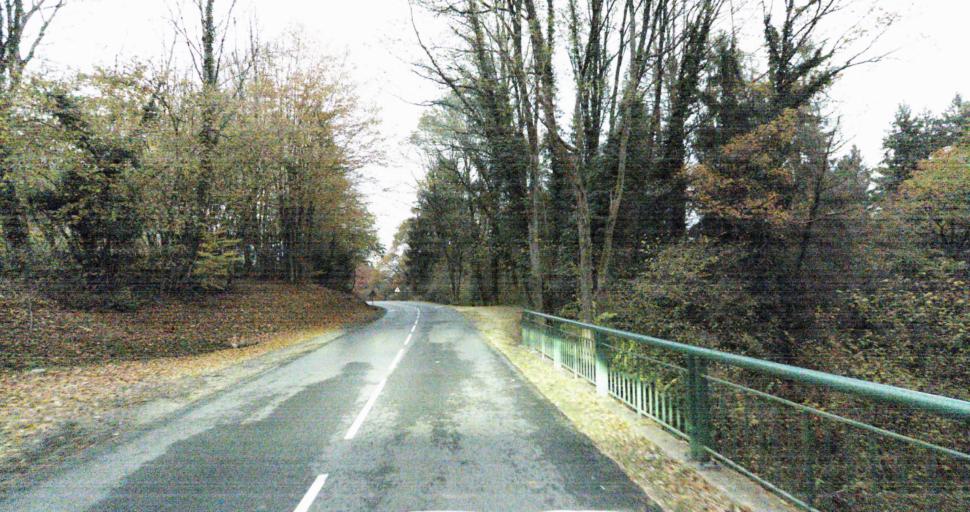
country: FR
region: Rhone-Alpes
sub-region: Departement de la Haute-Savoie
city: Sevrier
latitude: 45.8431
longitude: 6.1380
